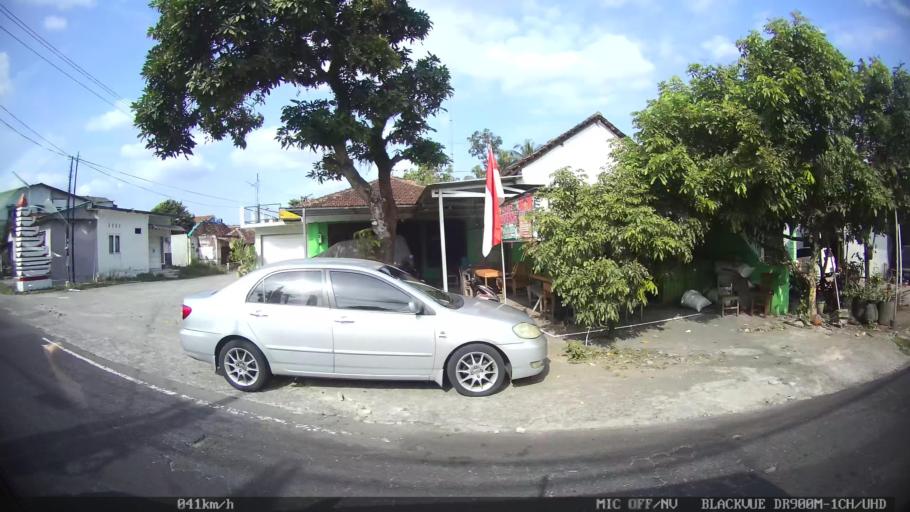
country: ID
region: Daerah Istimewa Yogyakarta
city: Depok
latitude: -7.7248
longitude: 110.4350
